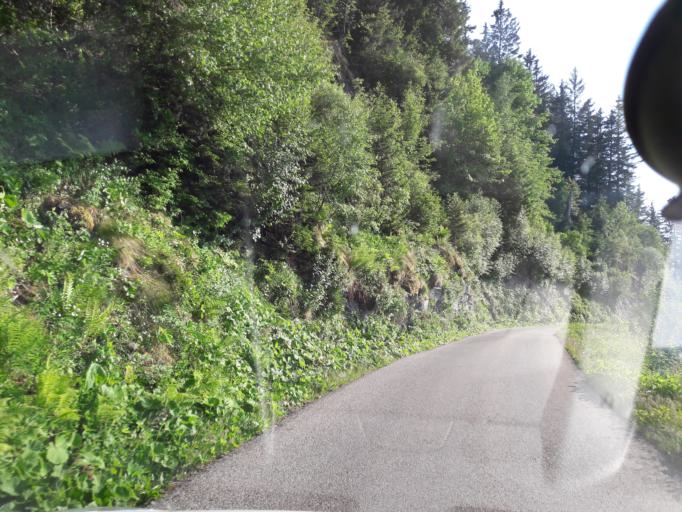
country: FR
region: Rhone-Alpes
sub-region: Departement de l'Isere
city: Livet-et-Gavet
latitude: 45.0522
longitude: 5.8865
